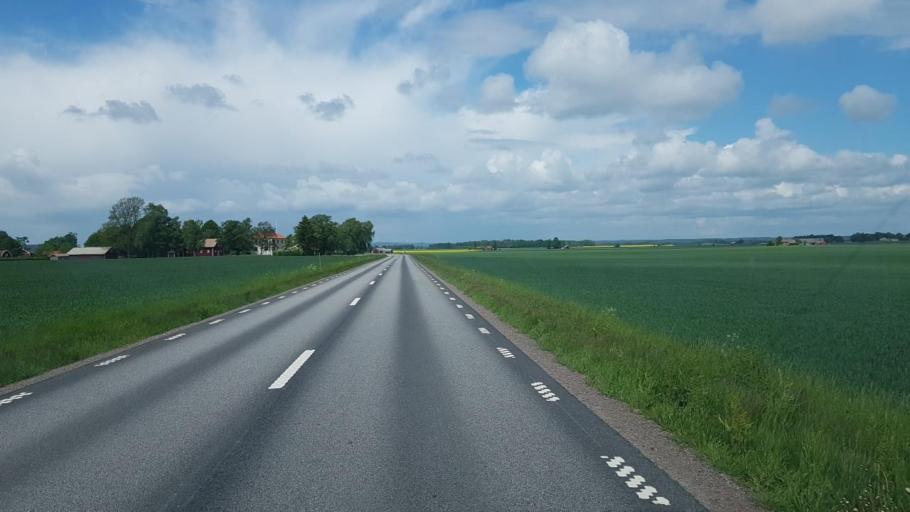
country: SE
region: OEstergoetland
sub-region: Motala Kommun
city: Borensberg
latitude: 58.5082
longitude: 15.1973
